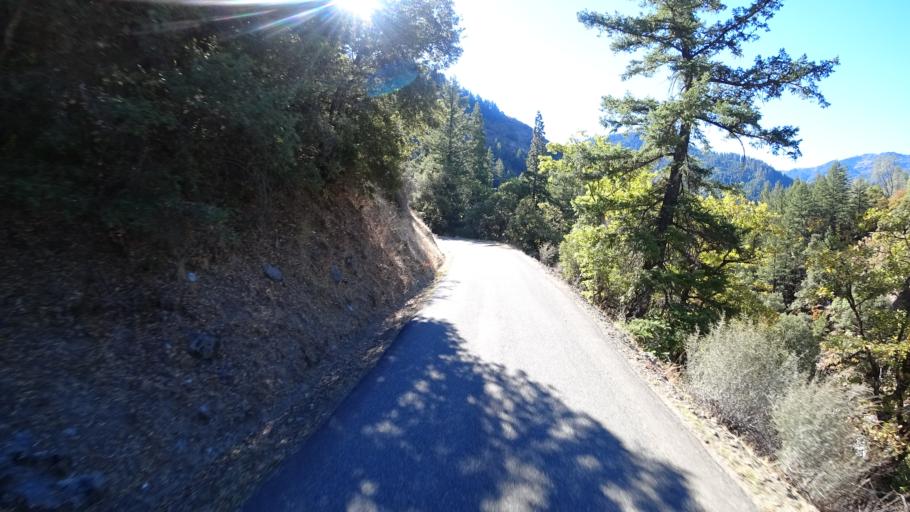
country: US
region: California
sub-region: Humboldt County
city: Willow Creek
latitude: 41.1605
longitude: -123.2078
